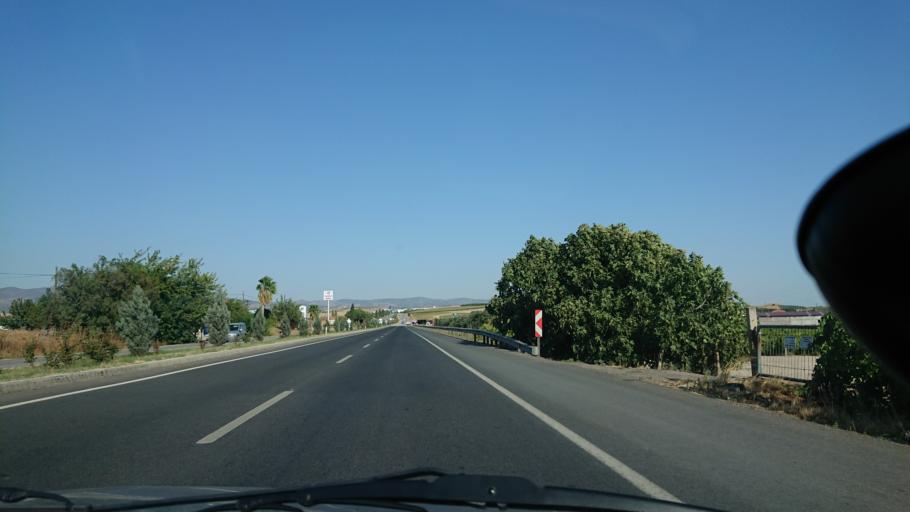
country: TR
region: Manisa
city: Adala
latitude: 38.5099
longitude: 28.2953
